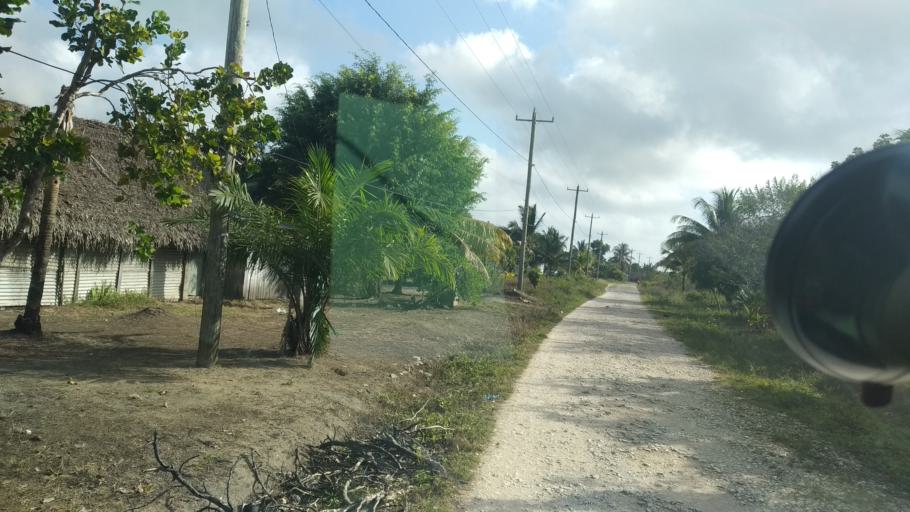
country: BZ
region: Stann Creek
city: Placencia
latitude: 16.5074
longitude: -88.5491
